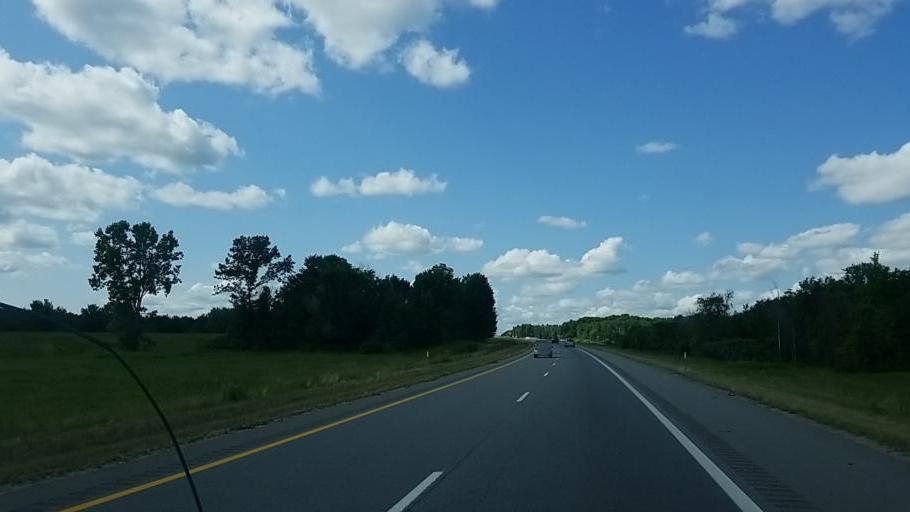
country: US
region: Michigan
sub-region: Mecosta County
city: Big Rapids
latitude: 43.6230
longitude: -85.4989
